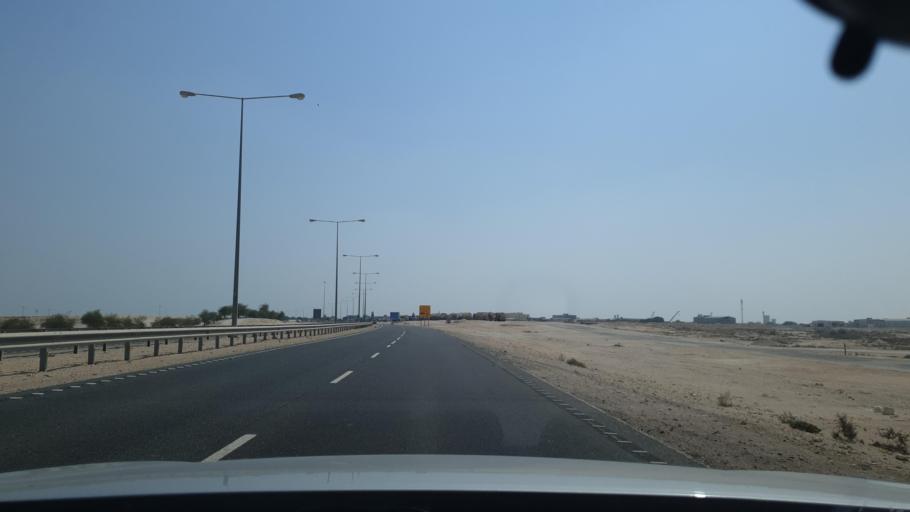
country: QA
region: Al Khawr
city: Al Khawr
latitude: 25.7258
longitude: 51.4968
